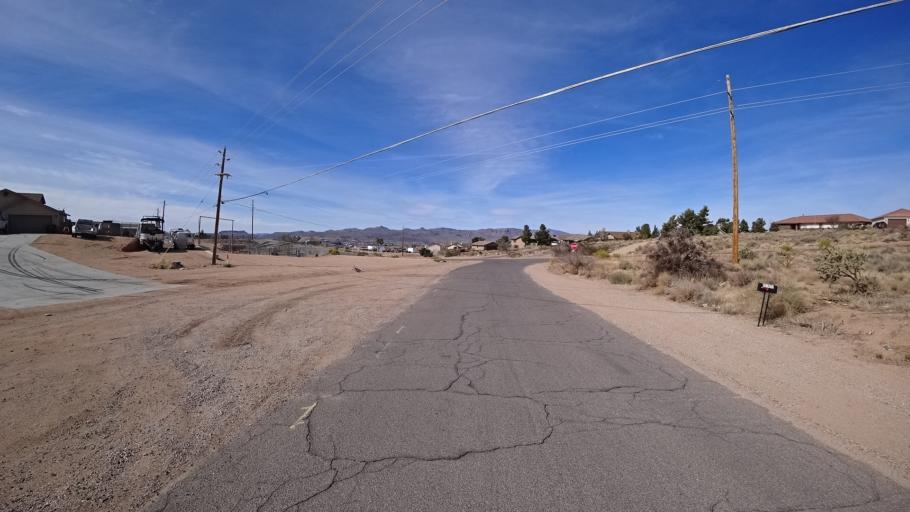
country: US
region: Arizona
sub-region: Mohave County
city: Kingman
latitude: 35.1810
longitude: -113.9902
